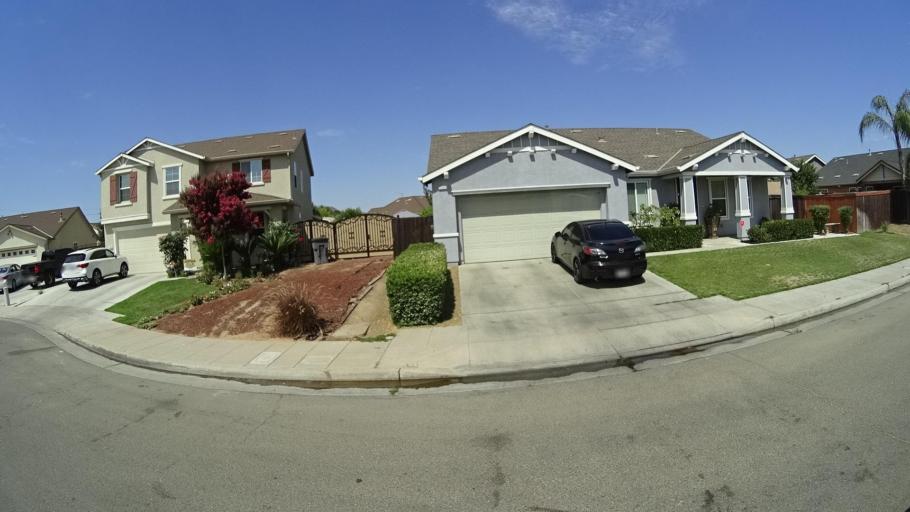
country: US
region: California
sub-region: Fresno County
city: Sunnyside
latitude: 36.7162
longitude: -119.7118
